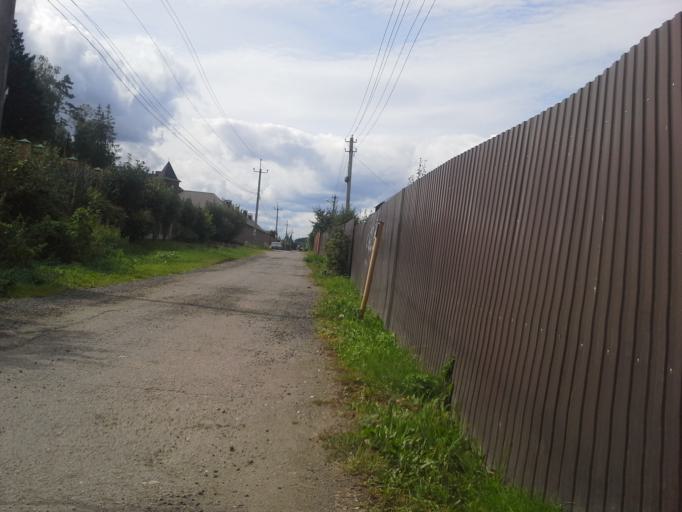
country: RU
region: Moskovskaya
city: Filimonki
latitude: 55.5443
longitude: 37.3821
